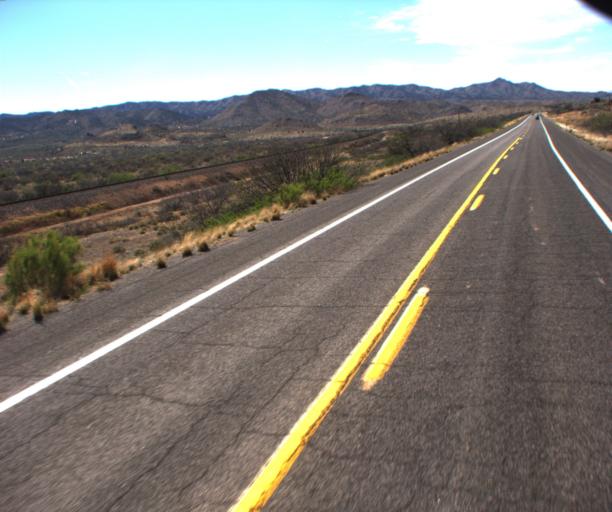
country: US
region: Arizona
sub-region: Mohave County
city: Peach Springs
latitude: 35.3619
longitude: -113.6958
